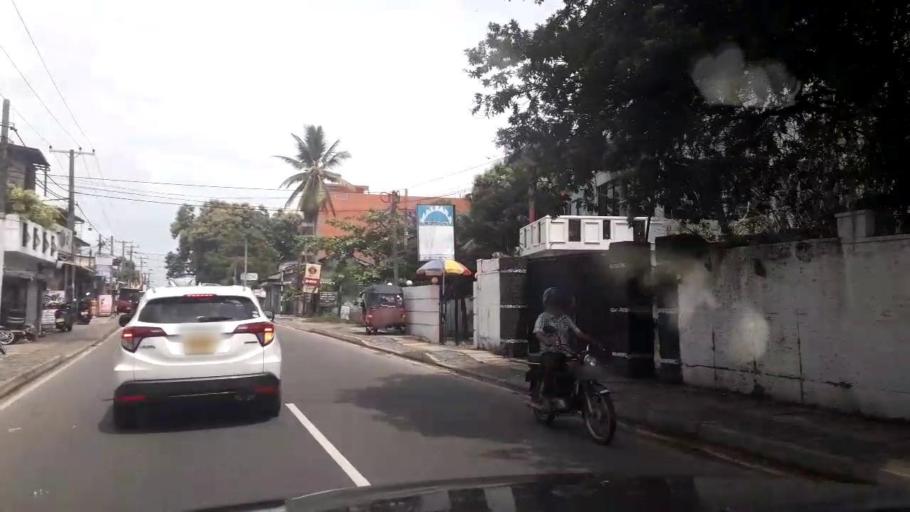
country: LK
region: Western
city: Moratuwa
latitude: 6.7511
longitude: 79.9001
